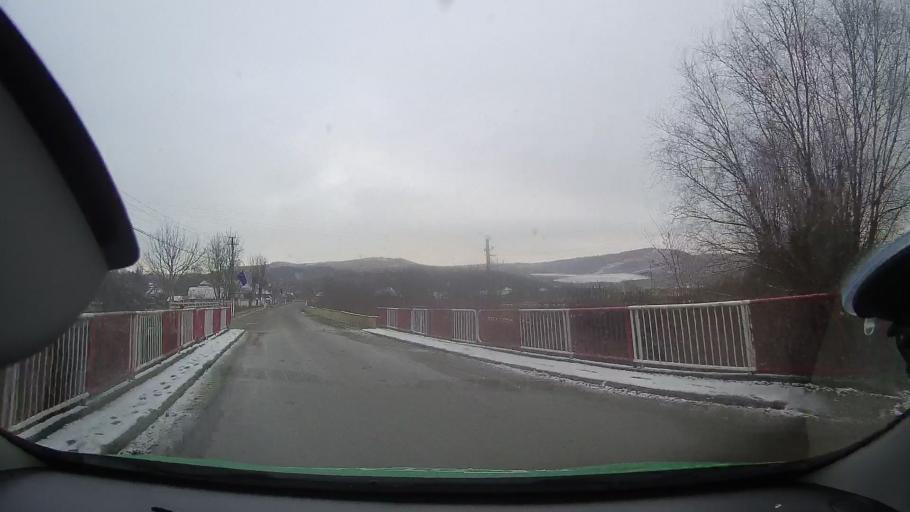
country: RO
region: Alba
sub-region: Comuna Farau
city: Farau
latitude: 46.3391
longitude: 24.0050
